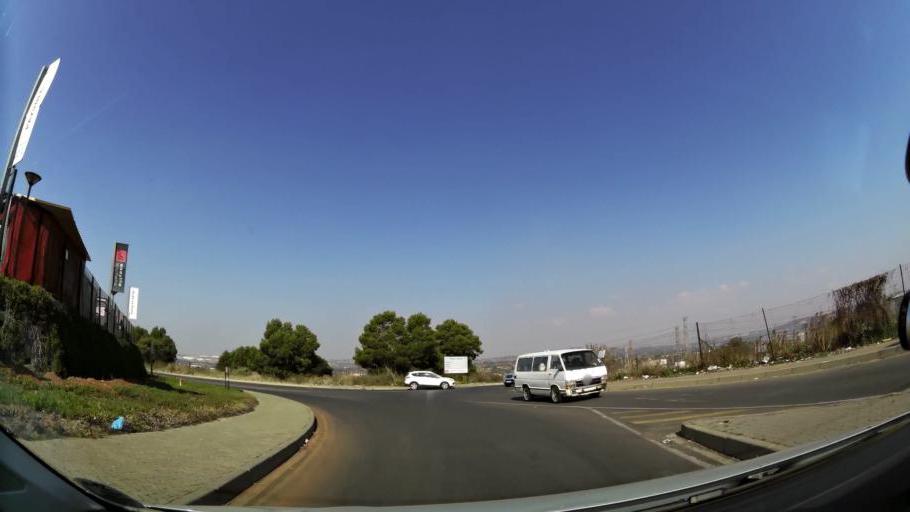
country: ZA
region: Gauteng
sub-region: City of Johannesburg Metropolitan Municipality
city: Modderfontein
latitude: -26.1227
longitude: 28.1421
